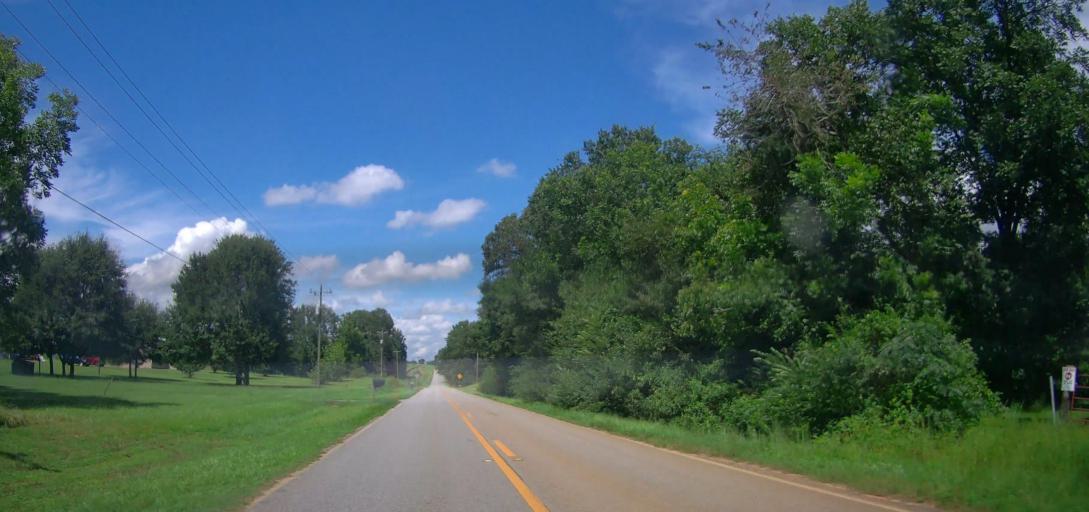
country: US
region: Georgia
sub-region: Peach County
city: Fort Valley
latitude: 32.5041
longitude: -83.8647
